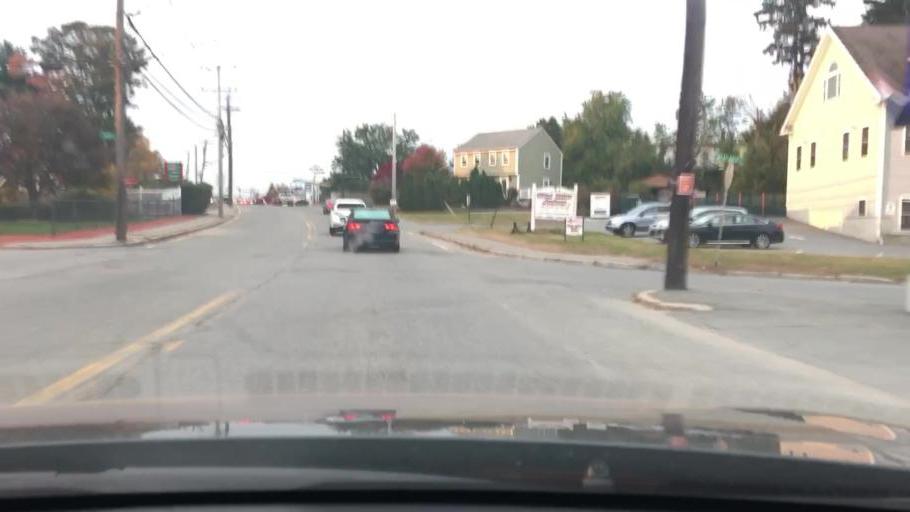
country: US
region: Massachusetts
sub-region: Essex County
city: North Andover
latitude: 42.7324
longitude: -71.1356
